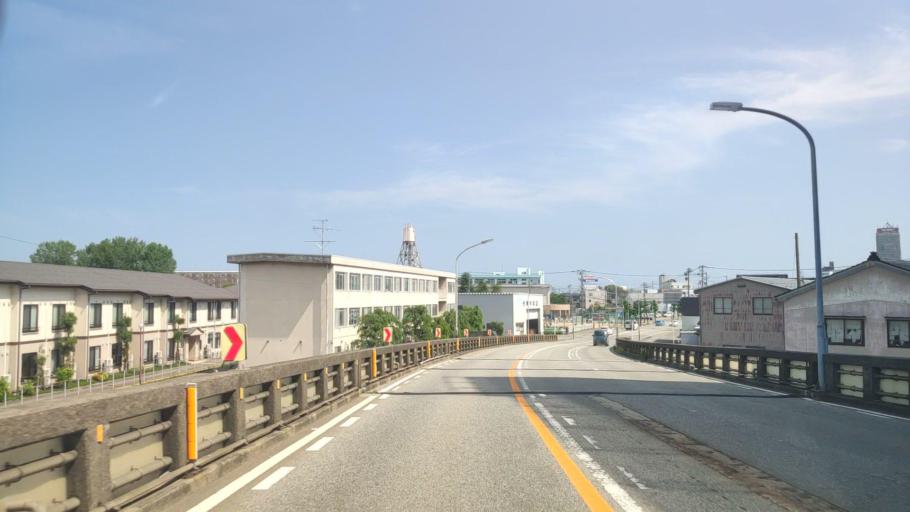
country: JP
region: Toyama
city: Toyama-shi
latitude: 36.6994
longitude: 137.2259
